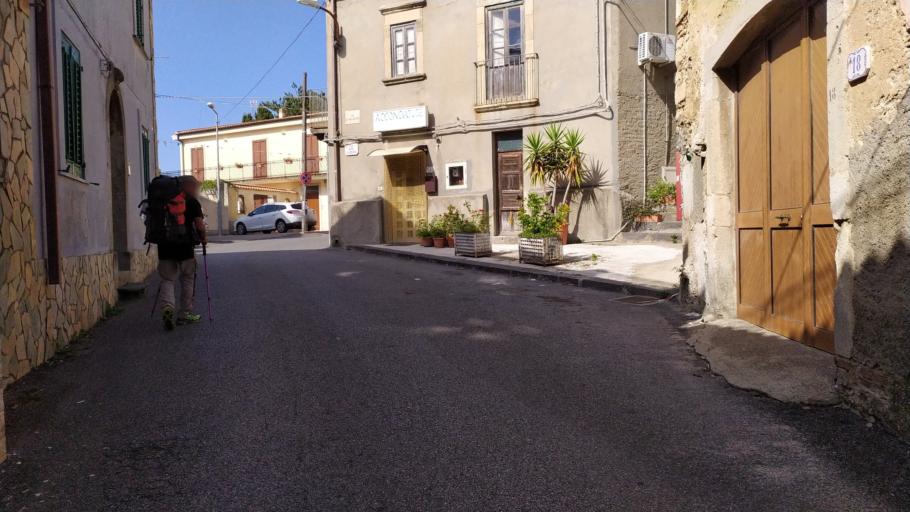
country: IT
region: Sicily
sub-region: Messina
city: Rometta
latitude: 38.1699
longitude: 15.4140
